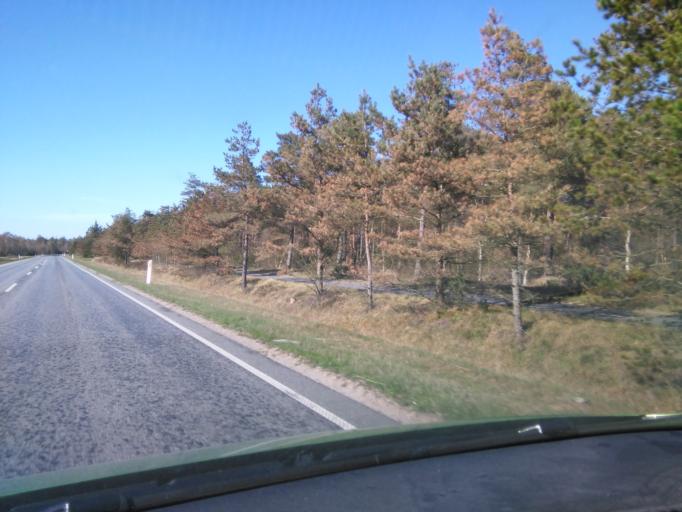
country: DK
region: South Denmark
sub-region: Varde Kommune
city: Oksbol
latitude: 55.5975
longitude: 8.2255
